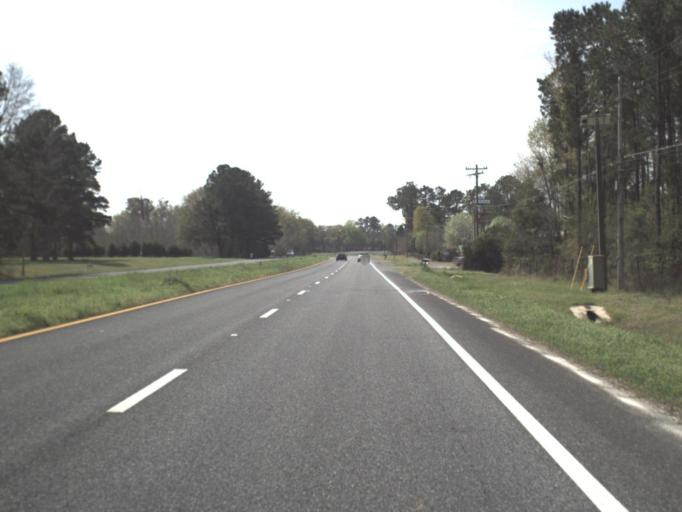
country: US
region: Florida
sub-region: Gadsden County
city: Havana
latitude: 30.6830
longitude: -84.3827
